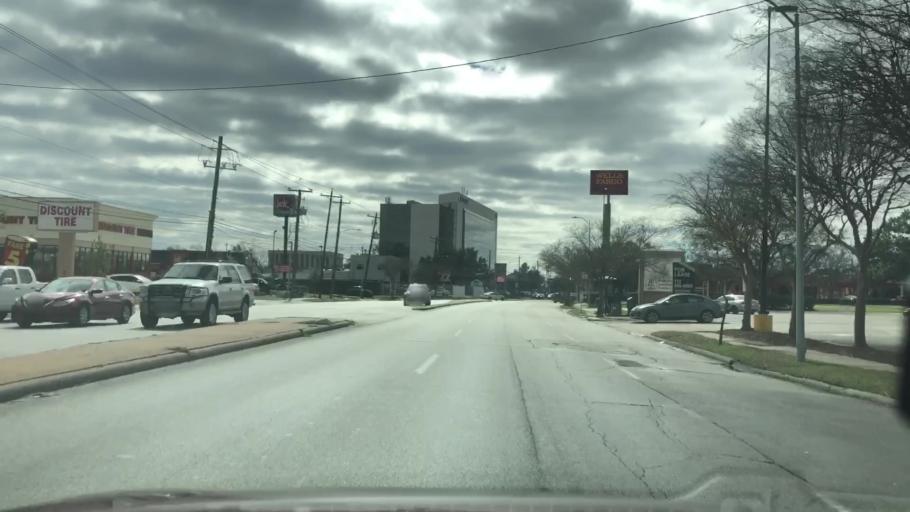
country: US
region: Texas
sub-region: Harris County
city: Piney Point Village
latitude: 29.7368
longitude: -95.5010
